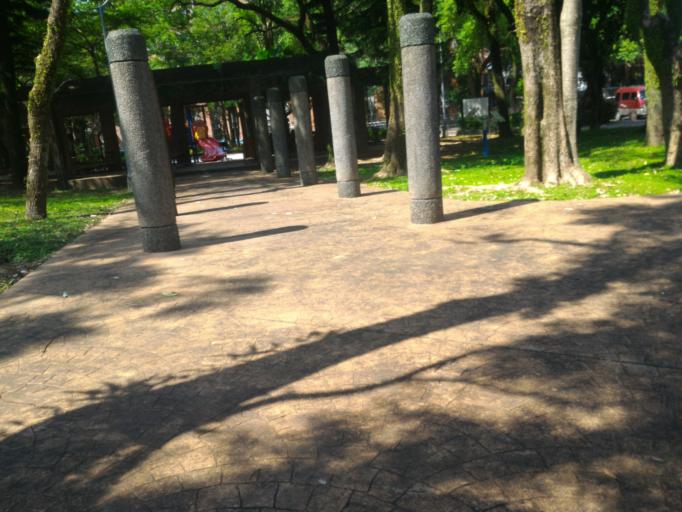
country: TW
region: Taipei
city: Taipei
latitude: 25.0384
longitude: 121.6160
